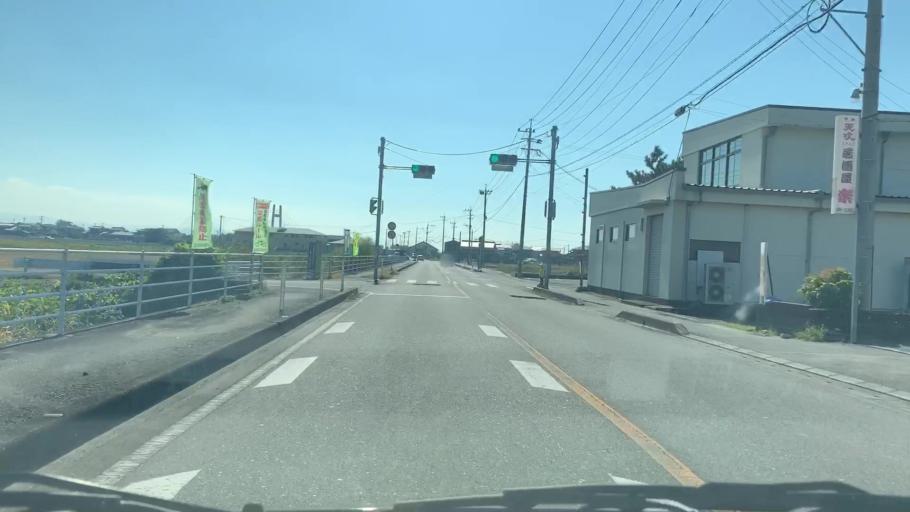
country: JP
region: Saga Prefecture
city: Kanzakimachi-kanzaki
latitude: 33.2927
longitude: 130.4454
